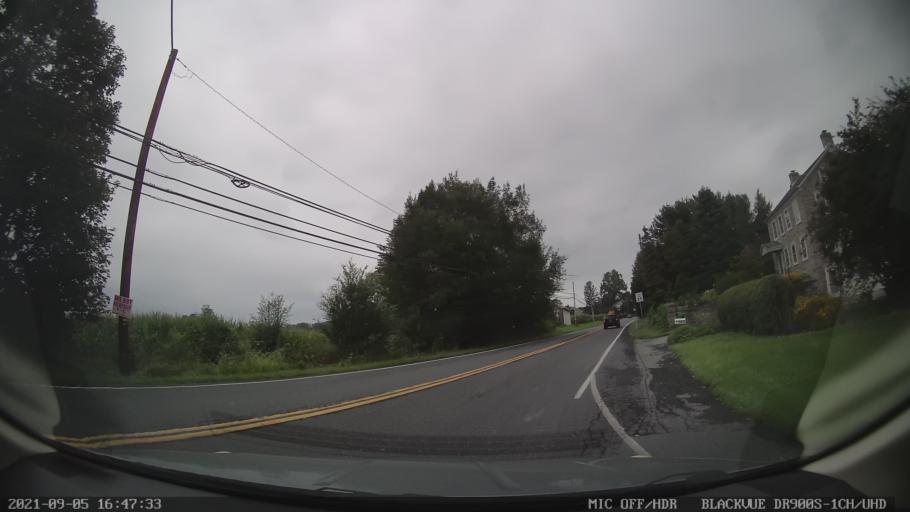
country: US
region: Pennsylvania
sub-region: Lehigh County
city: Stiles
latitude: 40.6484
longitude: -75.5343
